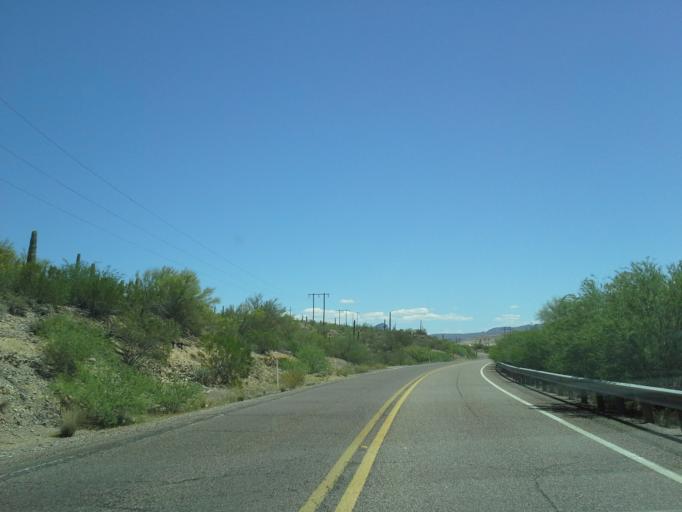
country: US
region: Arizona
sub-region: Pinal County
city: Kearny
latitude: 33.0163
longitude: -110.8414
